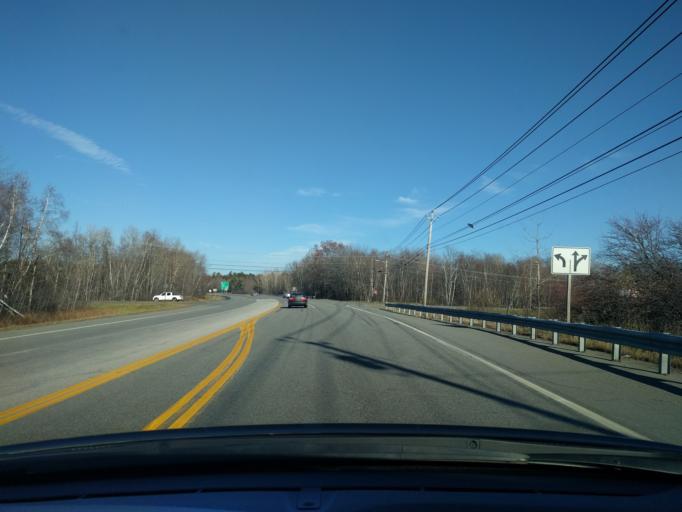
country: US
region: Maine
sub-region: Penobscot County
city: Bangor
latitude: 44.7783
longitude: -68.7978
